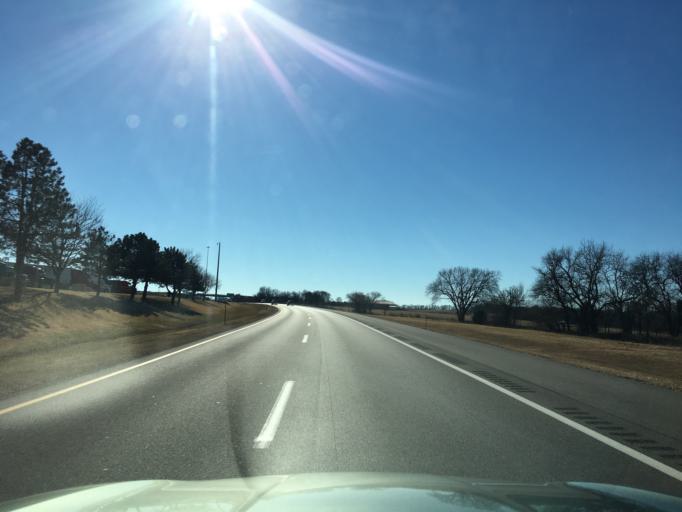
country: US
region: Kansas
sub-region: Sumner County
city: Belle Plaine
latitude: 37.3677
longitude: -97.3235
